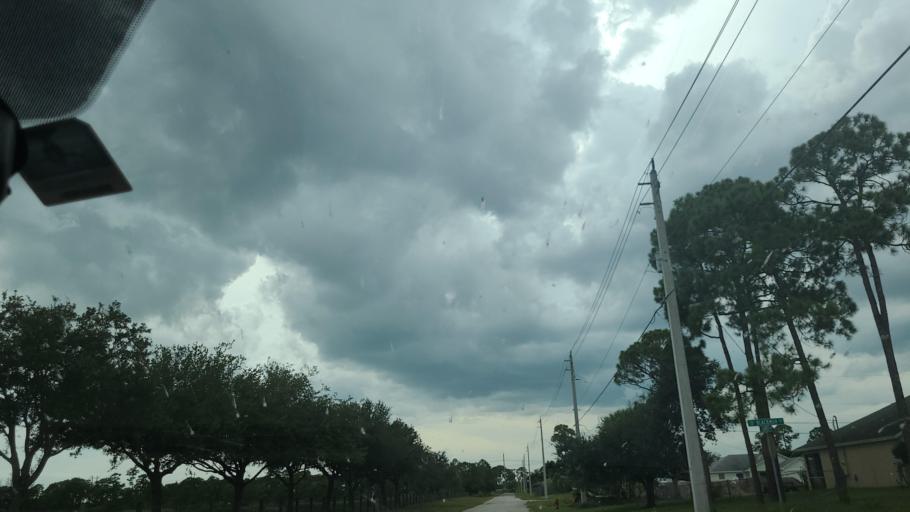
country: US
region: Florida
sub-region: Saint Lucie County
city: Port Saint Lucie
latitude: 27.2499
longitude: -80.4107
